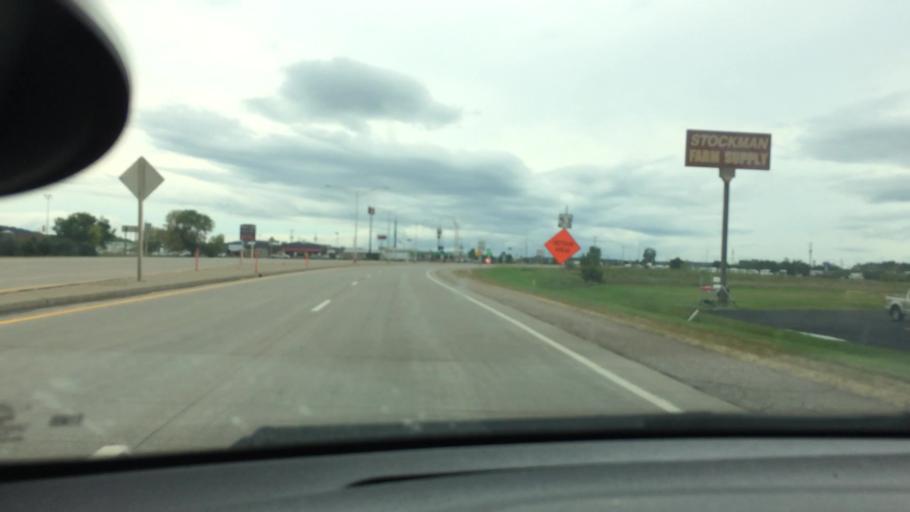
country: US
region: Wisconsin
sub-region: Trempealeau County
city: Osseo
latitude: 44.5806
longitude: -91.1971
